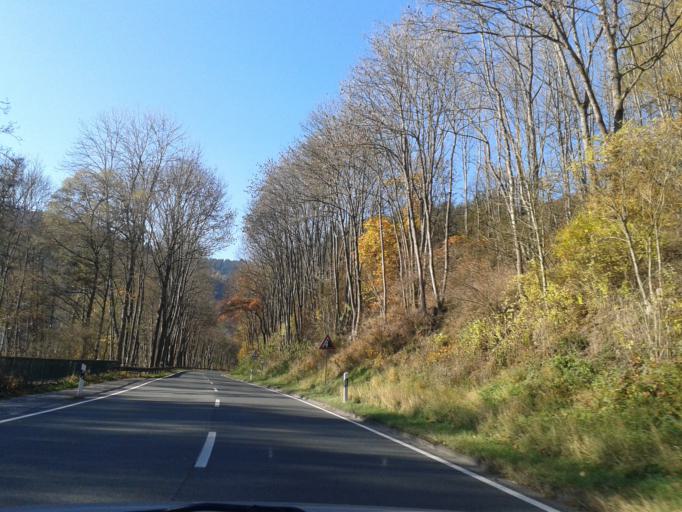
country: DE
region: North Rhine-Westphalia
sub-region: Regierungsbezirk Arnsberg
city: Bad Laasphe
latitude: 50.9236
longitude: 8.4009
